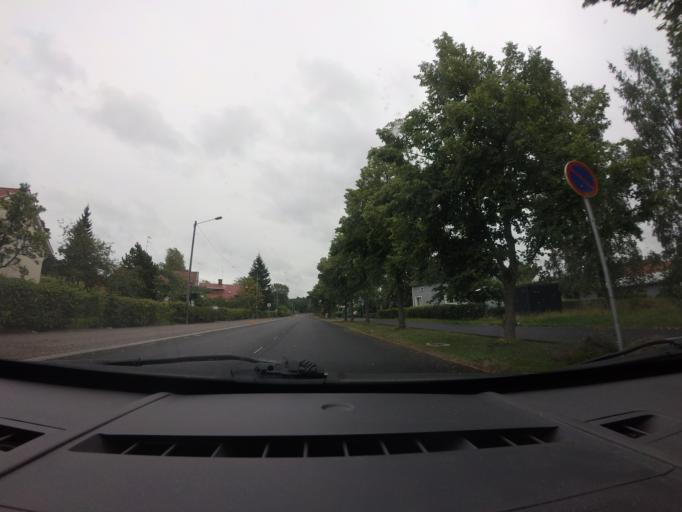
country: FI
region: Varsinais-Suomi
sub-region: Turku
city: Turku
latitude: 60.4352
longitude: 22.2750
